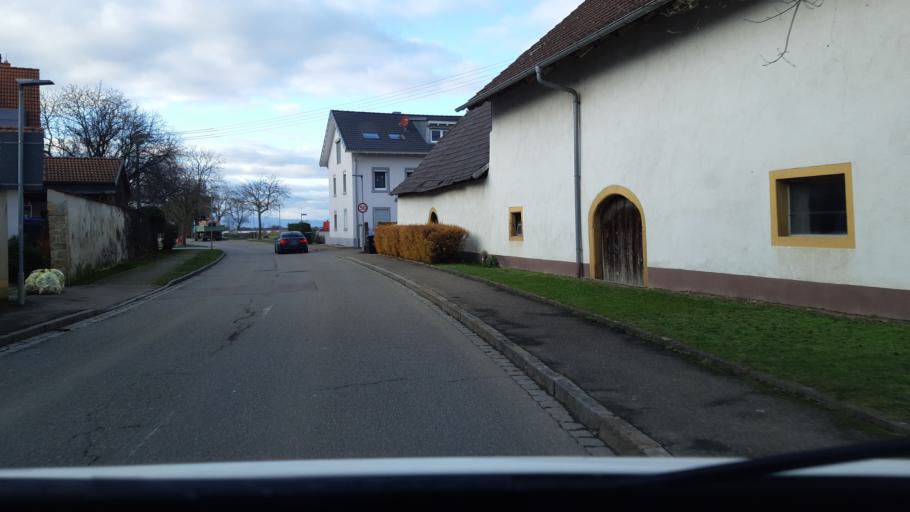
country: DE
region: Baden-Wuerttemberg
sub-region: Freiburg Region
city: Eschbach
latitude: 47.9037
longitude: 7.6631
